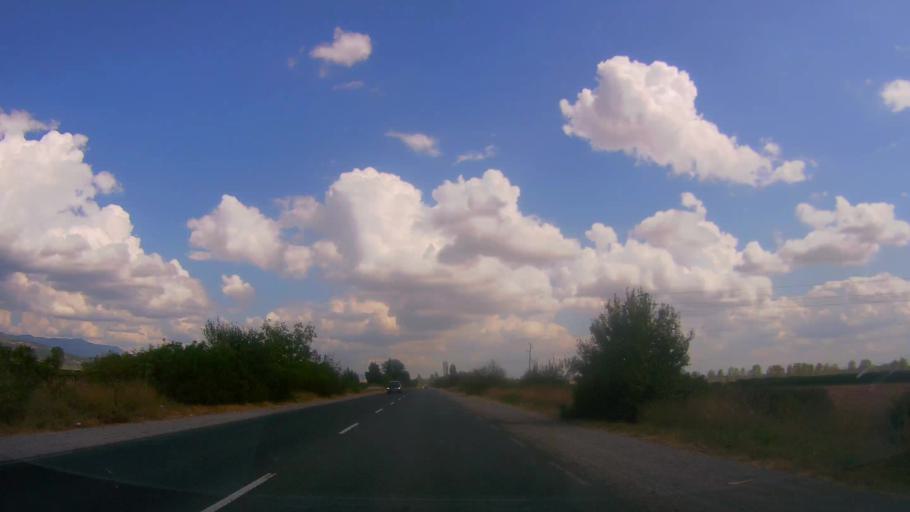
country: BG
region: Sliven
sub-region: Obshtina Sliven
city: Sliven
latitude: 42.6366
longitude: 26.2341
